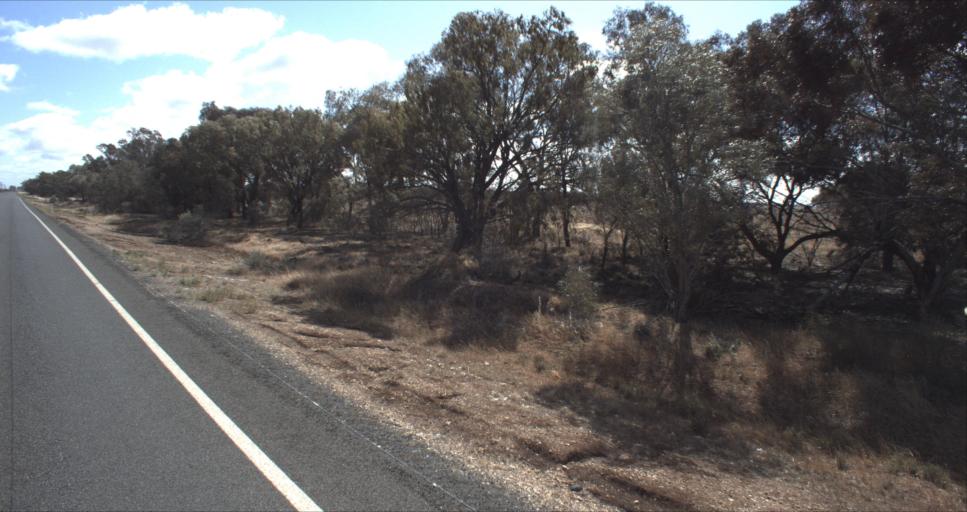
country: AU
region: New South Wales
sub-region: Murrumbidgee Shire
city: Darlington Point
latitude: -34.5284
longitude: 146.1744
